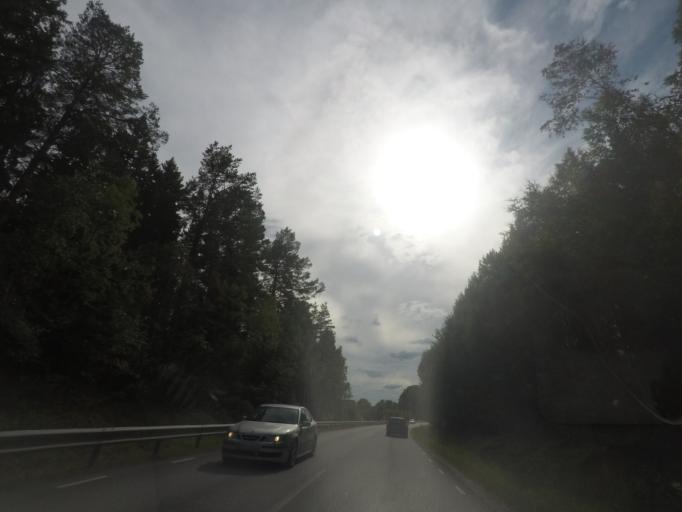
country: SE
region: Stockholm
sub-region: Norrtalje Kommun
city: Skanninge
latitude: 59.9032
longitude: 18.5755
